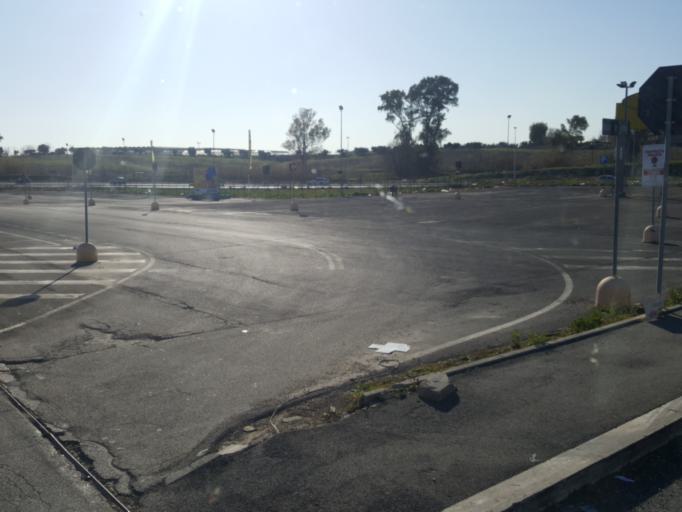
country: IT
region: Latium
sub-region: Citta metropolitana di Roma Capitale
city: Setteville
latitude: 41.8867
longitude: 12.6052
